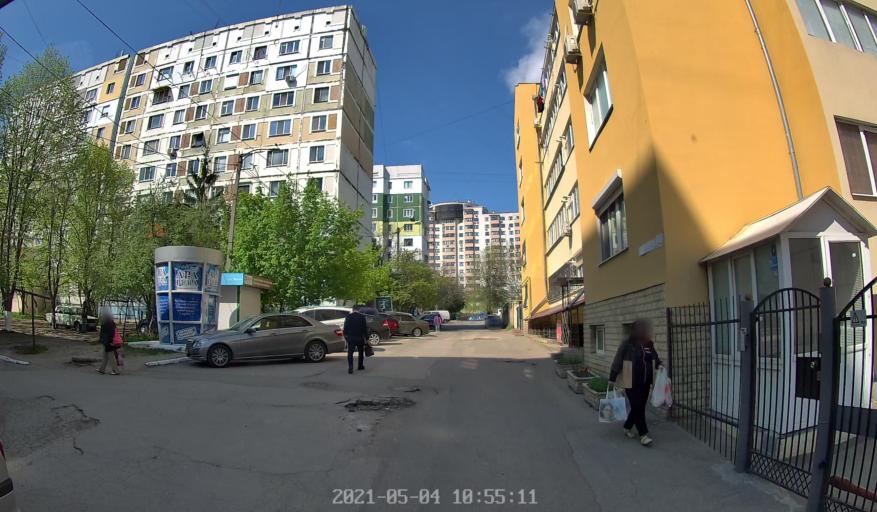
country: MD
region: Chisinau
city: Chisinau
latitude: 47.0468
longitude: 28.8854
